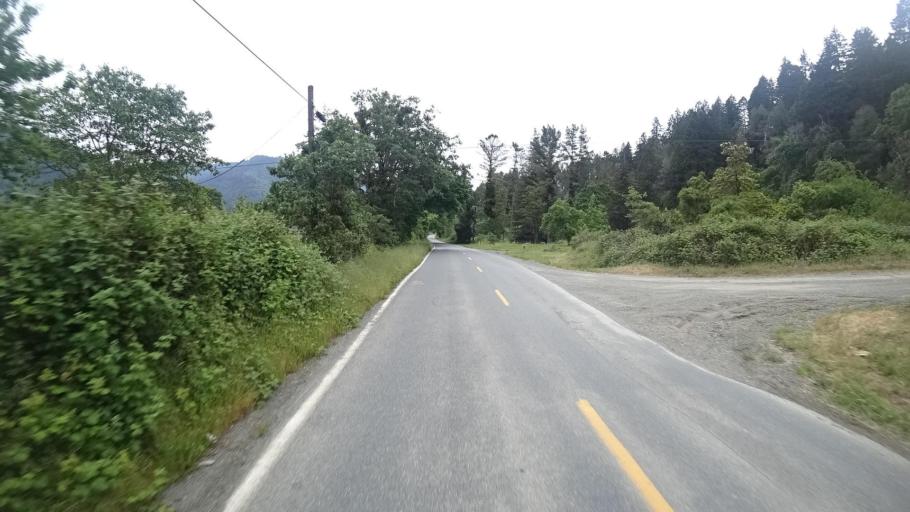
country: US
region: California
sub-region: Humboldt County
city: Willow Creek
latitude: 41.0786
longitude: -123.6987
